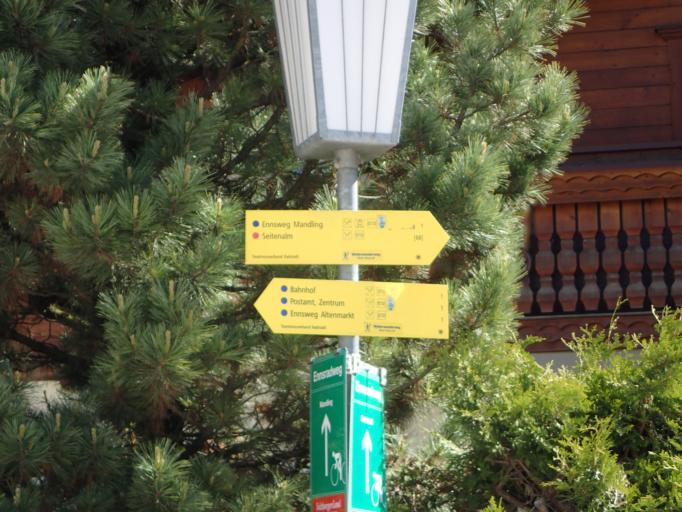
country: AT
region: Salzburg
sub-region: Politischer Bezirk Sankt Johann im Pongau
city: Radstadt
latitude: 47.3819
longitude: 13.4753
